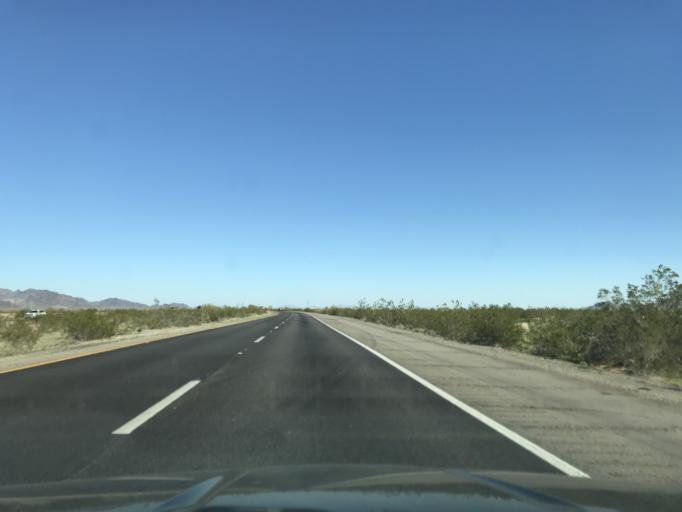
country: US
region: California
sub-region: Riverside County
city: Mesa Verde
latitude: 33.6057
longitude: -114.9279
